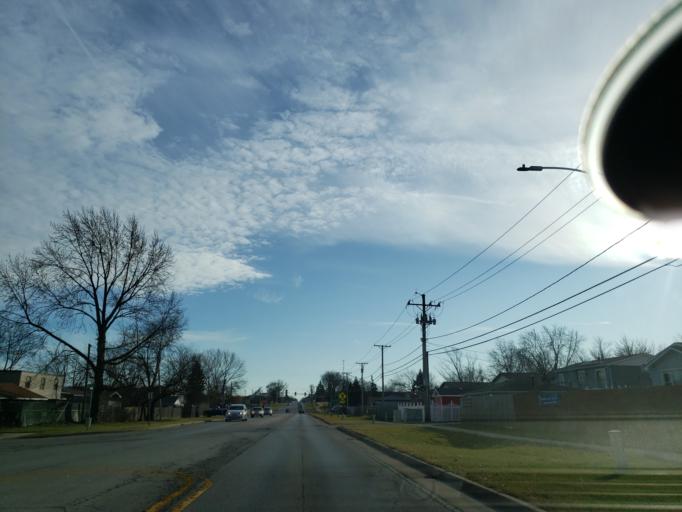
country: US
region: Illinois
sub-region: Cook County
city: Oak Forest
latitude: 41.6097
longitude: -87.7563
